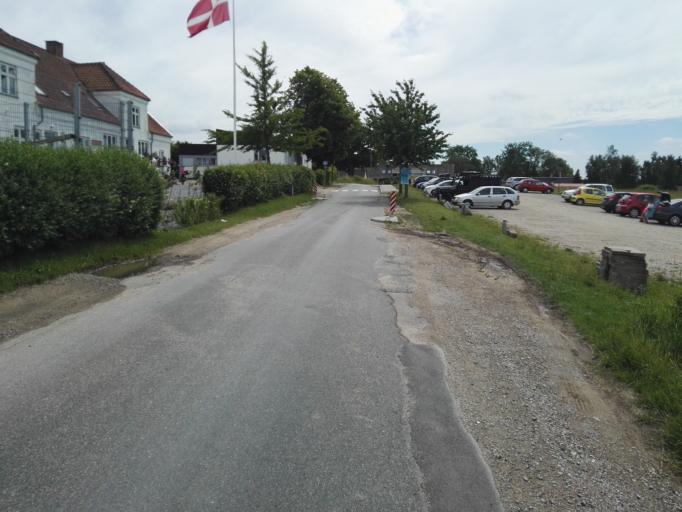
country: DK
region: Capital Region
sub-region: Hillerod Kommune
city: Skaevinge
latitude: 55.8847
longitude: 12.1303
